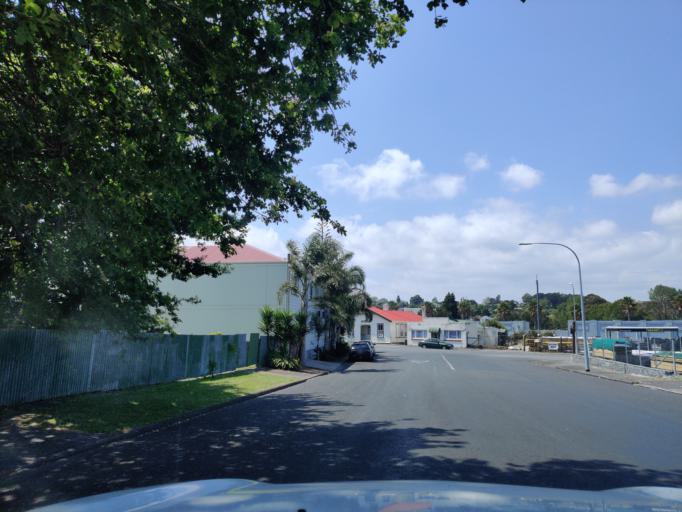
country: NZ
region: Auckland
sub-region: Auckland
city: Pukekohe East
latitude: -37.2582
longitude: 174.9477
